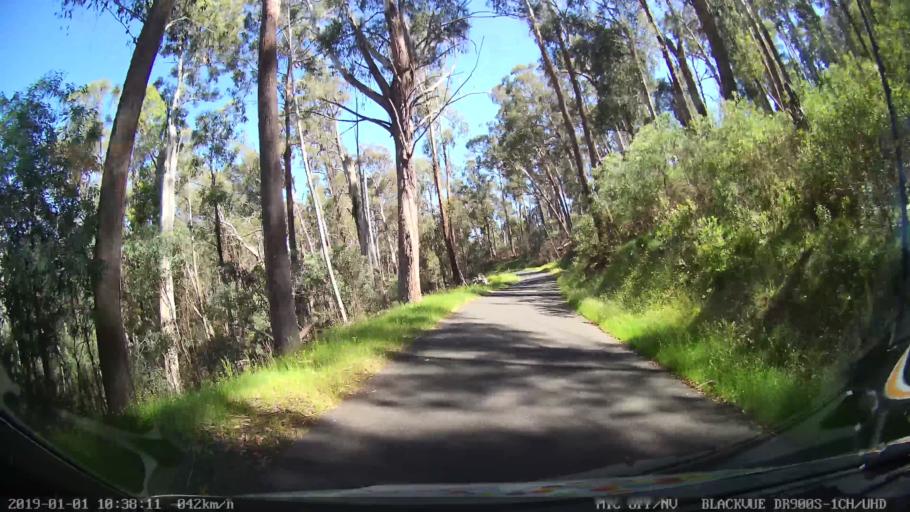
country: AU
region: New South Wales
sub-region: Snowy River
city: Jindabyne
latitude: -36.0466
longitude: 148.3018
